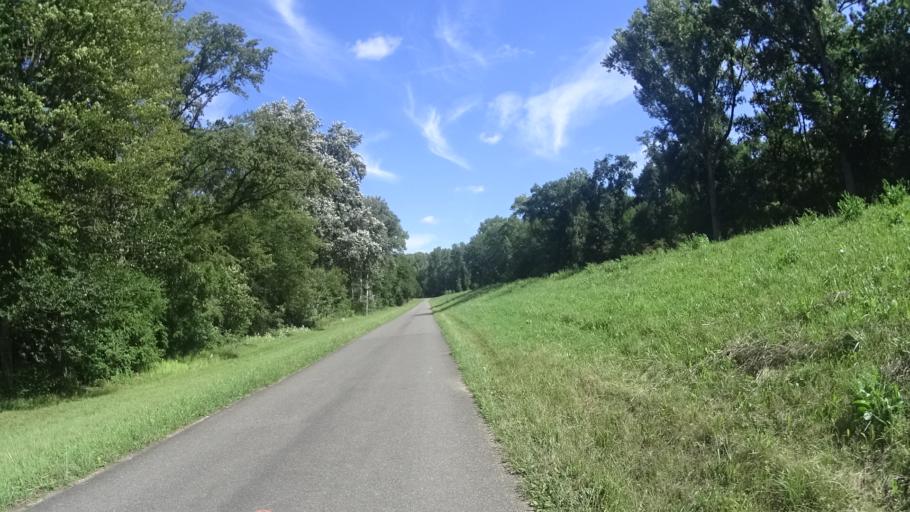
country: DE
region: Rheinland-Pfalz
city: Leimersheim
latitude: 49.1517
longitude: 8.3645
